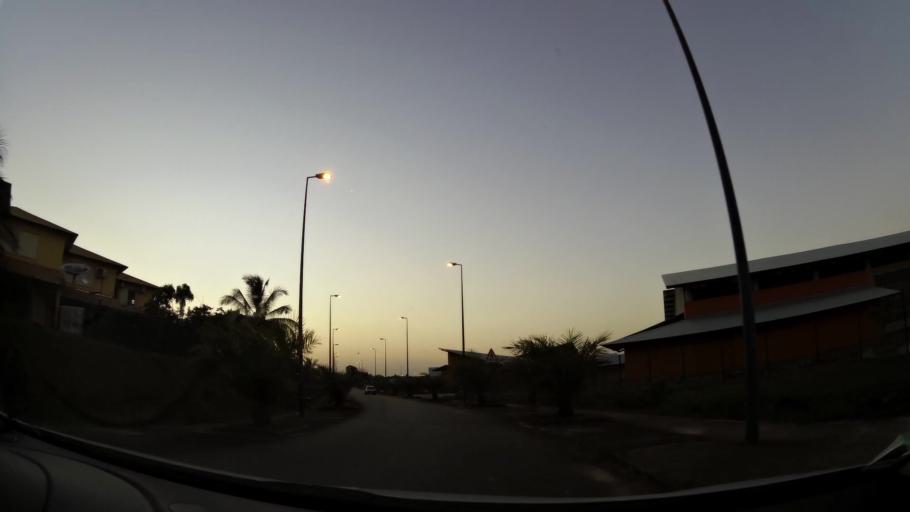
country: GF
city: Macouria
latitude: 4.9267
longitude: -52.4101
